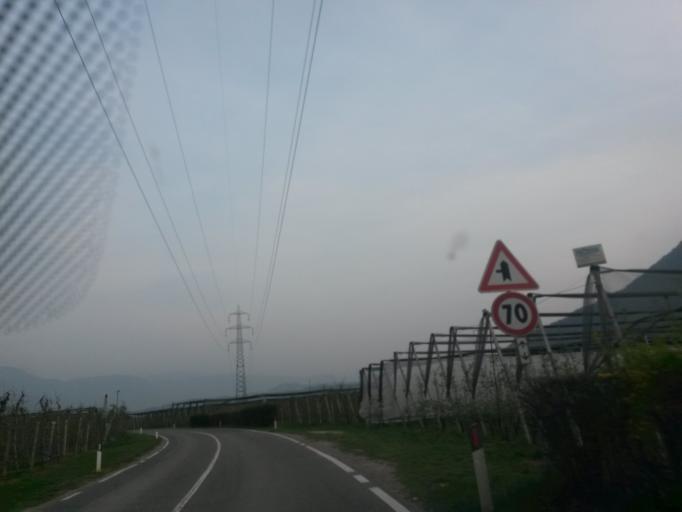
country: IT
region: Trentino-Alto Adige
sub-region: Bolzano
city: Andriano
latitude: 46.5179
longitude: 11.2453
